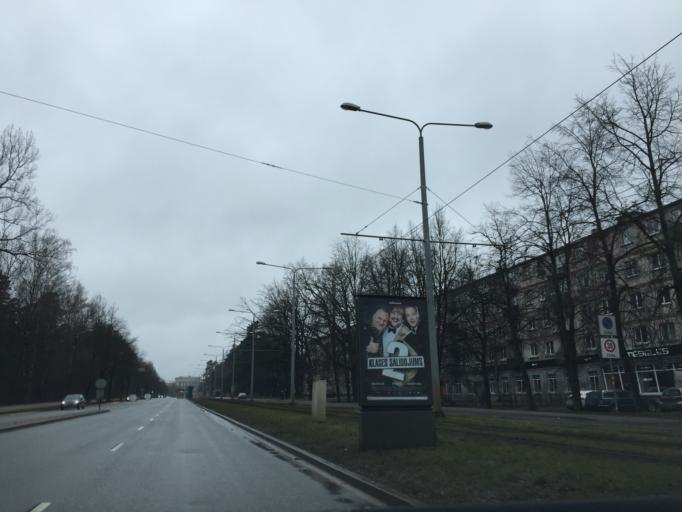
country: LV
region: Riga
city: Jaunciems
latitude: 56.9862
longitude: 24.2185
